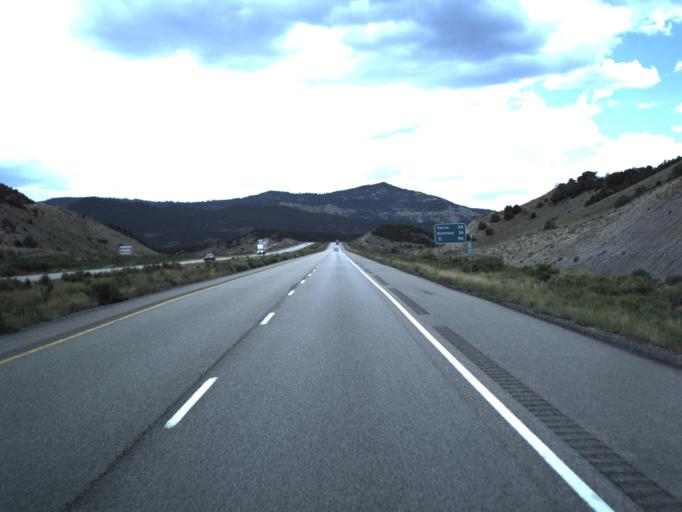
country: US
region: Utah
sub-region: Emery County
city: Ferron
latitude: 38.7614
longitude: -111.3670
